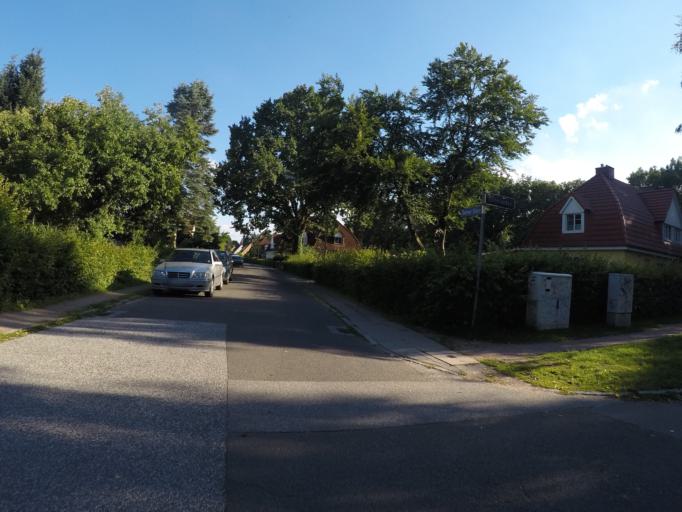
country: DE
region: Hamburg
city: Langenhorn
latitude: 53.6578
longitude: 10.0175
